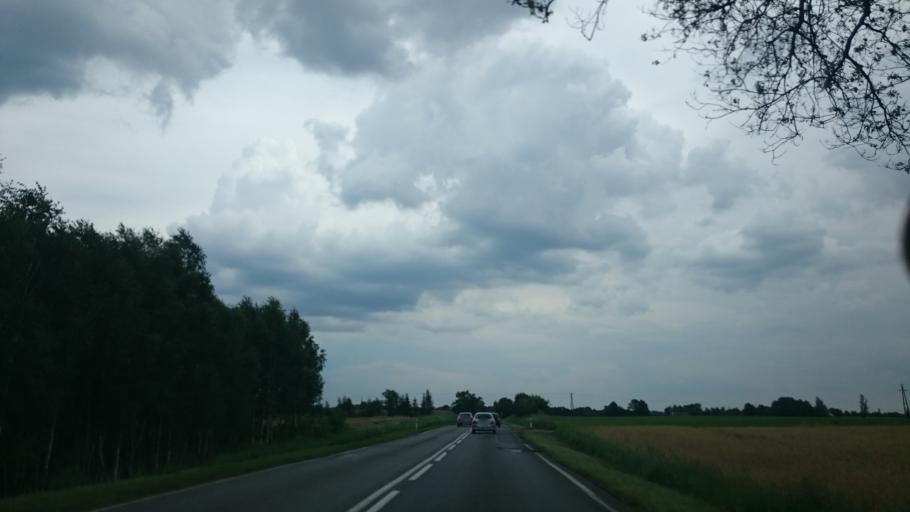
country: PL
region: Kujawsko-Pomorskie
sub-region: Powiat tucholski
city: Cekcyn
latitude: 53.5142
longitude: 17.9678
